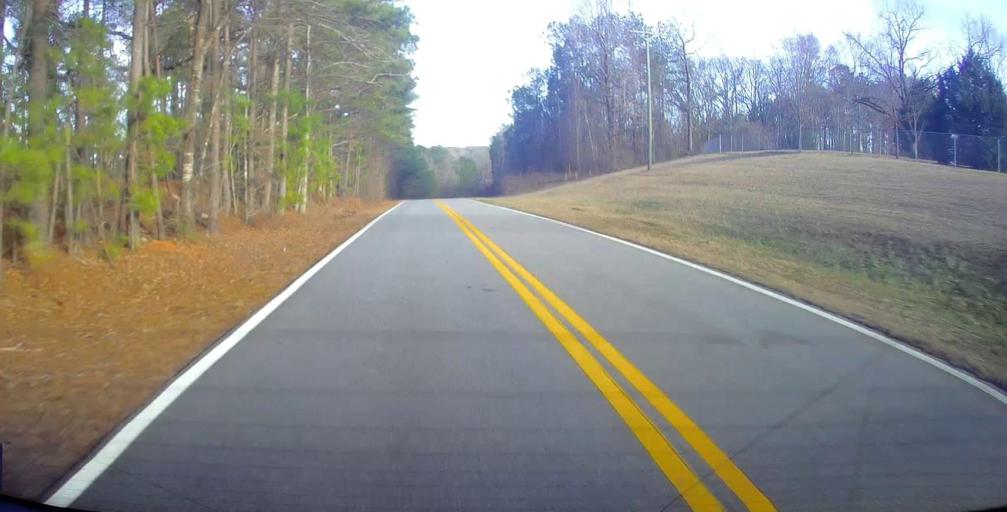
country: US
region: Georgia
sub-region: Bibb County
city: West Point
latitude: 32.8385
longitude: -83.9062
